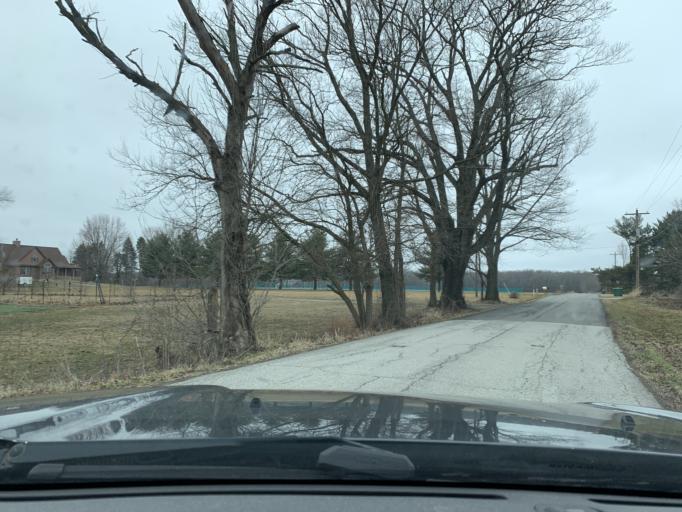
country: US
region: Indiana
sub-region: Porter County
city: Chesterton
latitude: 41.6070
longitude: -87.0044
